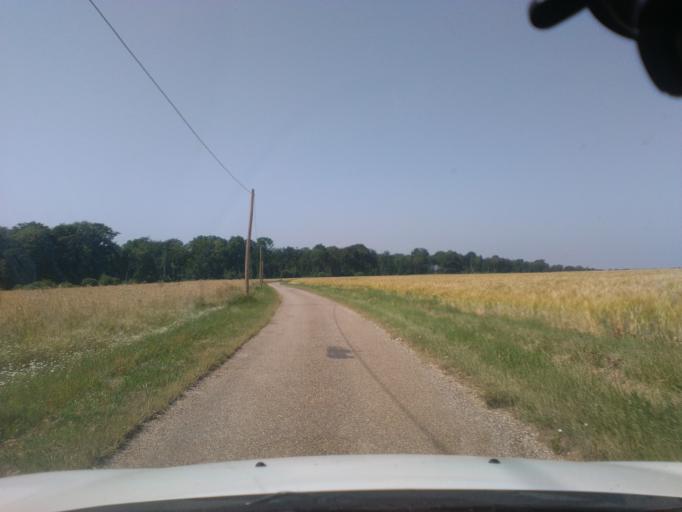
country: FR
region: Lorraine
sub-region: Departement des Vosges
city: Liffol-le-Grand
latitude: 48.3089
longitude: 5.4143
